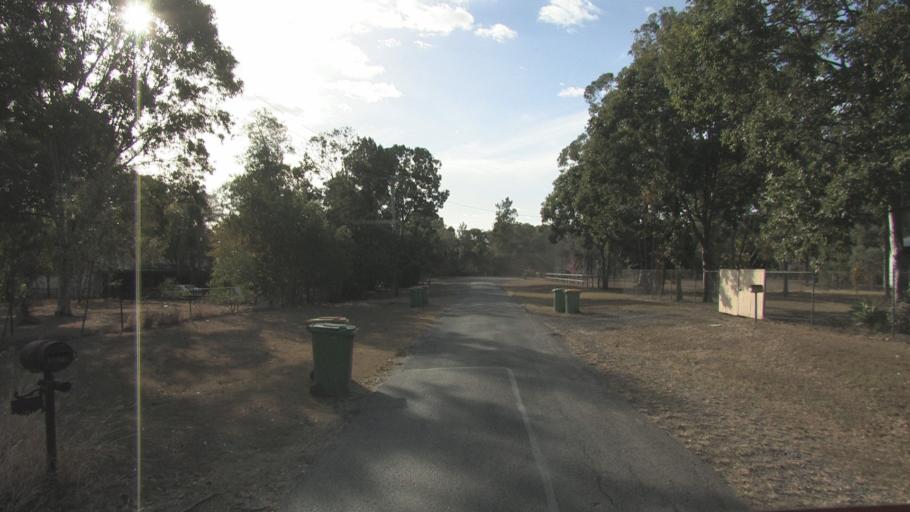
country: AU
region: Queensland
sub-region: Logan
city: Cedar Vale
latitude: -27.8784
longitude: 153.0209
